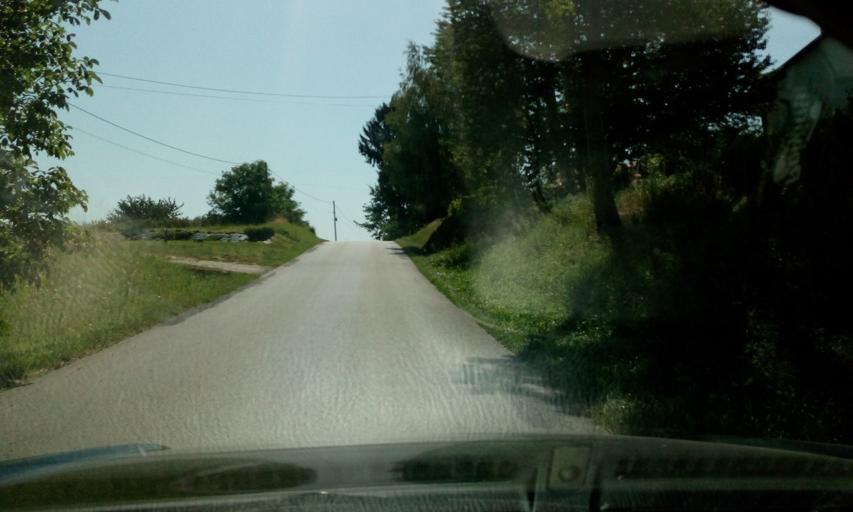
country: PL
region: Subcarpathian Voivodeship
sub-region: Powiat lancucki
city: Wysoka
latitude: 50.0488
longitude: 22.2403
